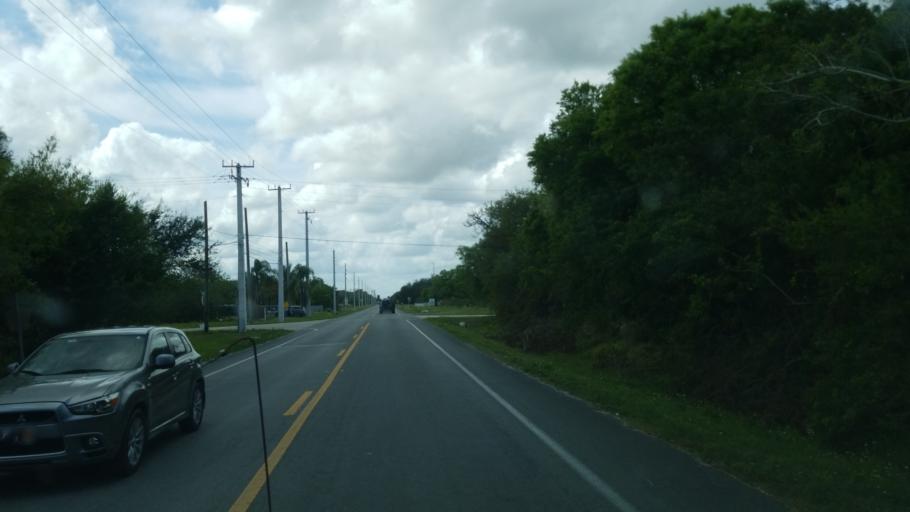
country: US
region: Florida
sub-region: Saint Lucie County
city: Lakewood Park
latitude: 27.4476
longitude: -80.4718
